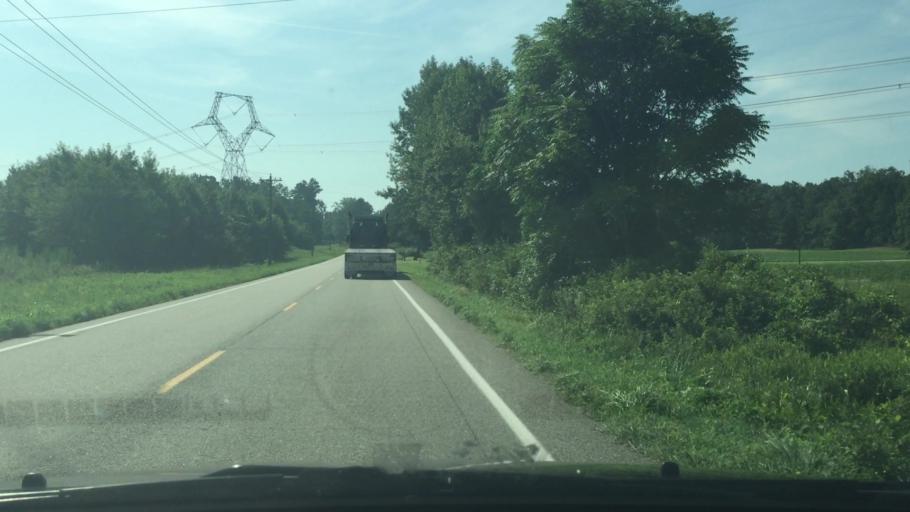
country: US
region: Virginia
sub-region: Sussex County
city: Sussex
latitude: 37.0595
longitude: -77.3290
